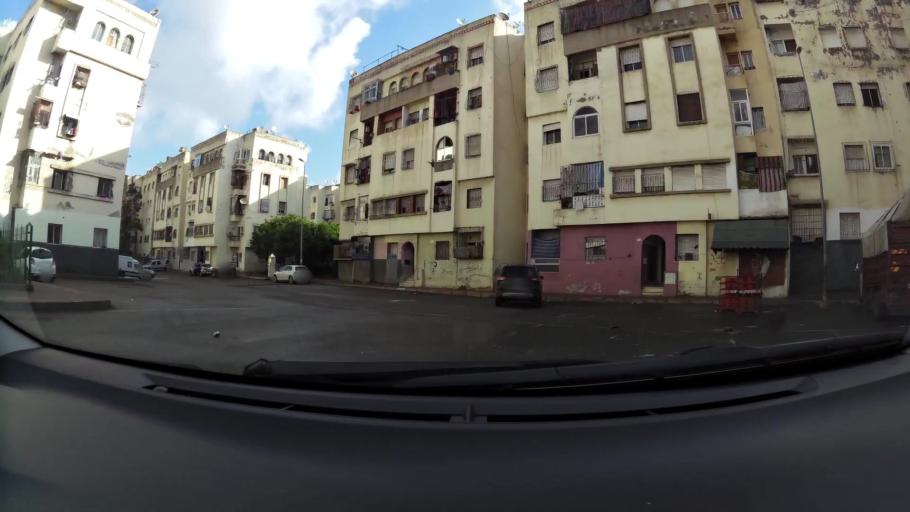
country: MA
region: Grand Casablanca
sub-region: Mediouna
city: Tit Mellil
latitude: 33.5973
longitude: -7.5345
